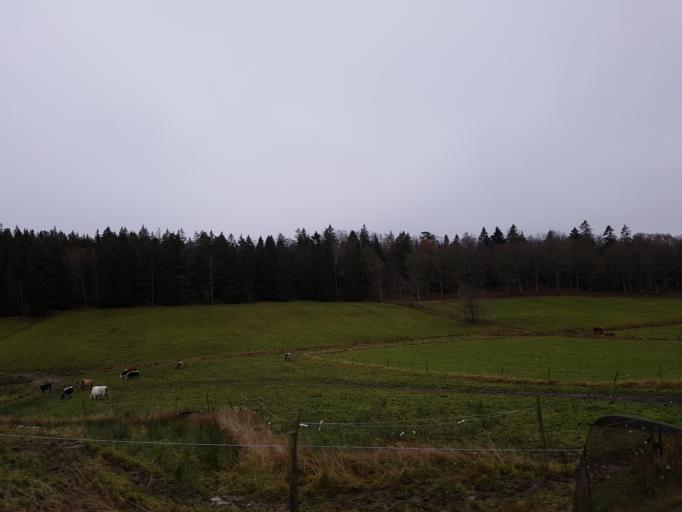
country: SE
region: Vaestra Goetaland
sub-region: Orust
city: Henan
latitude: 58.2021
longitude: 11.7534
